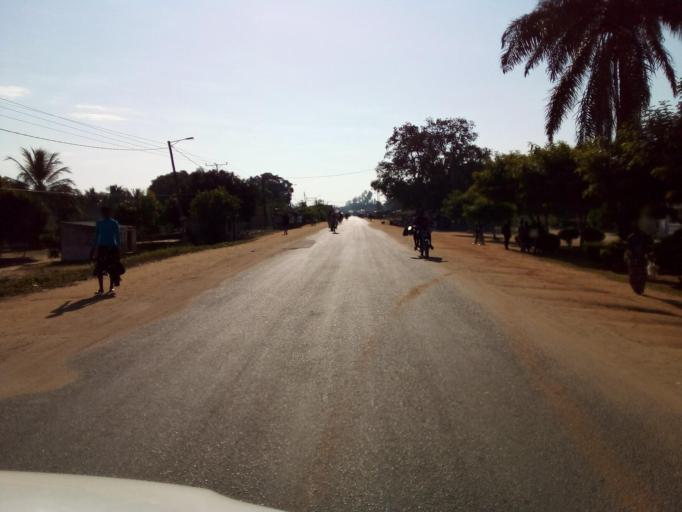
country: MZ
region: Zambezia
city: Quelimane
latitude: -17.5975
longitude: 36.8102
